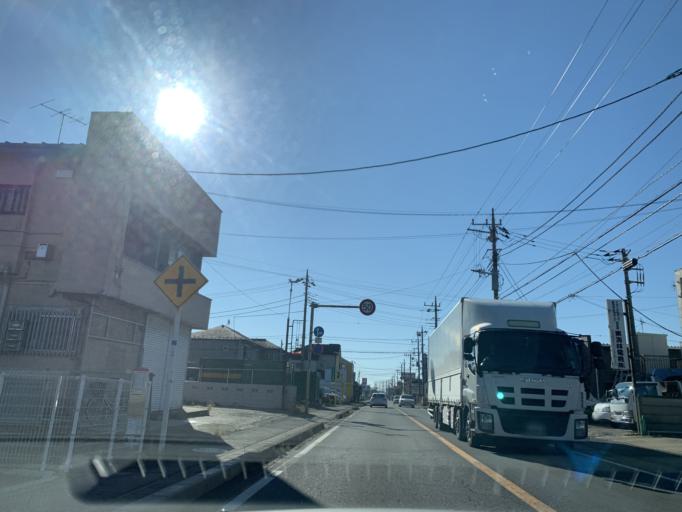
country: JP
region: Chiba
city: Matsudo
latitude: 35.8088
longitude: 139.8952
